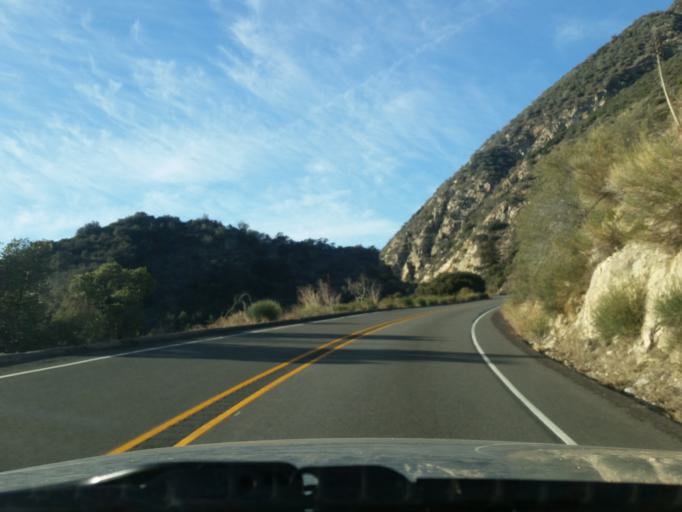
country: US
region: California
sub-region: San Bernardino County
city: Yucaipa
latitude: 34.0983
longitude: -116.9611
